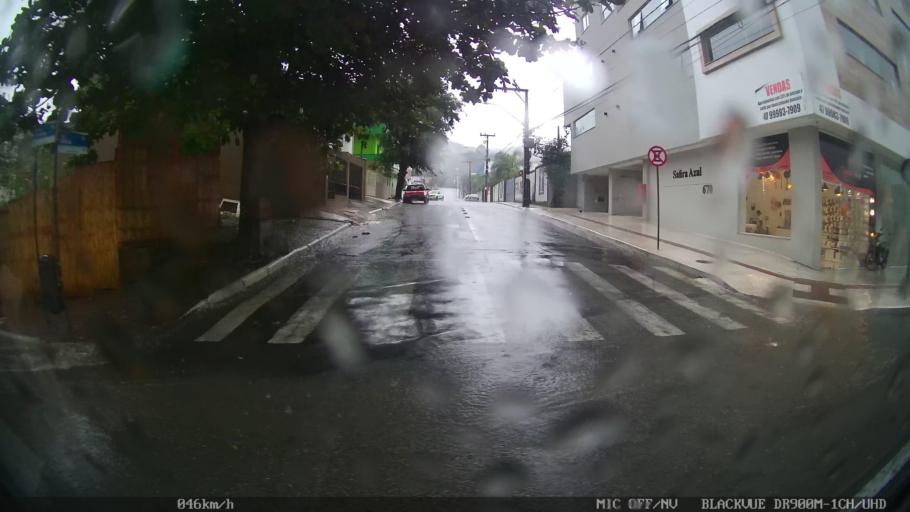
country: BR
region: Santa Catarina
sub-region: Balneario Camboriu
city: Balneario Camboriu
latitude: -26.9801
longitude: -48.6470
